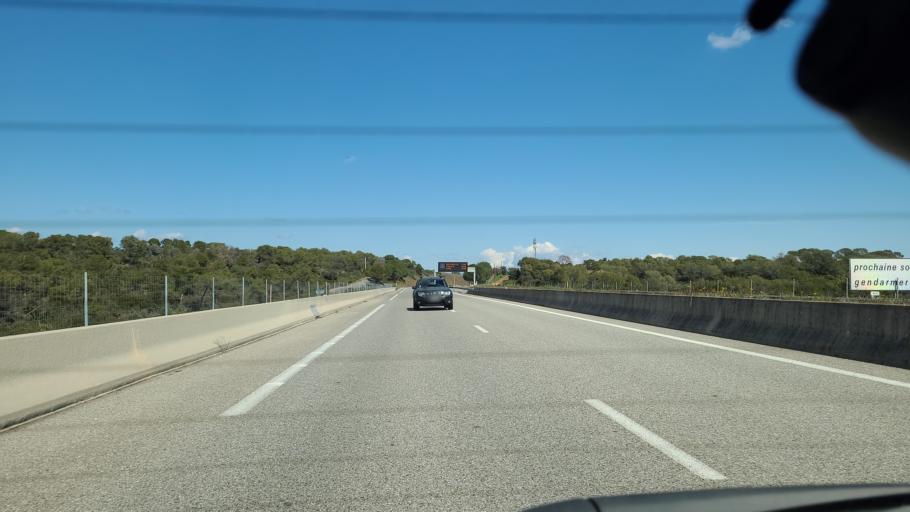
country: FR
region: Provence-Alpes-Cote d'Azur
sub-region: Departement du Var
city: Le Cannet-des-Maures
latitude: 43.3717
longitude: 6.3455
